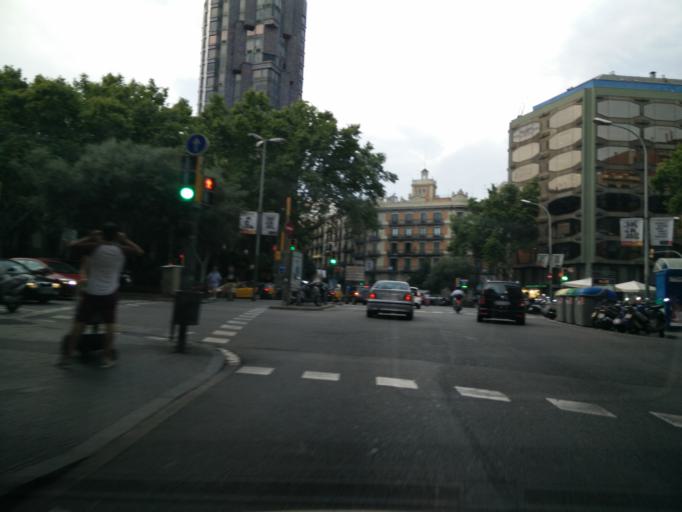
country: ES
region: Catalonia
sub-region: Provincia de Barcelona
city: Ciutat Vella
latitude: 41.3887
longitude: 2.1739
